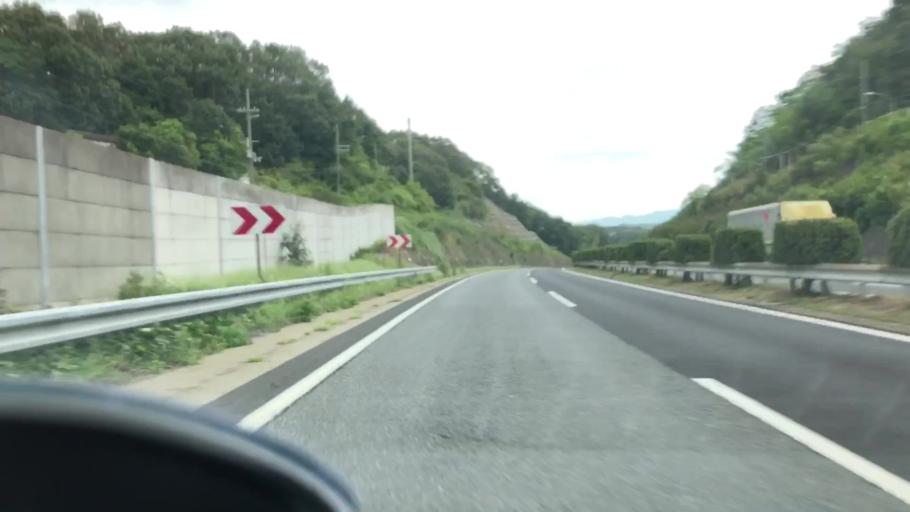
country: JP
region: Hyogo
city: Yashiro
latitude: 34.8919
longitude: 135.0906
